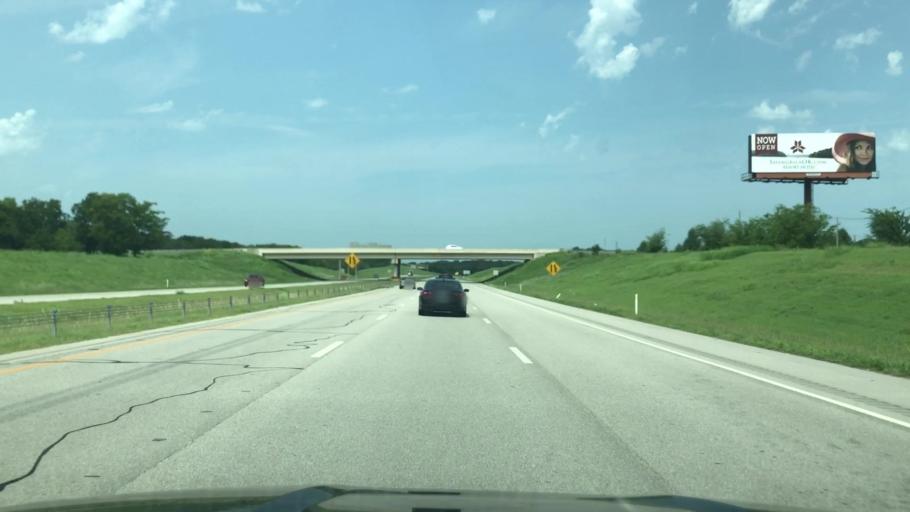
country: US
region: Oklahoma
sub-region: Rogers County
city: Catoosa
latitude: 36.1751
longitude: -95.7319
